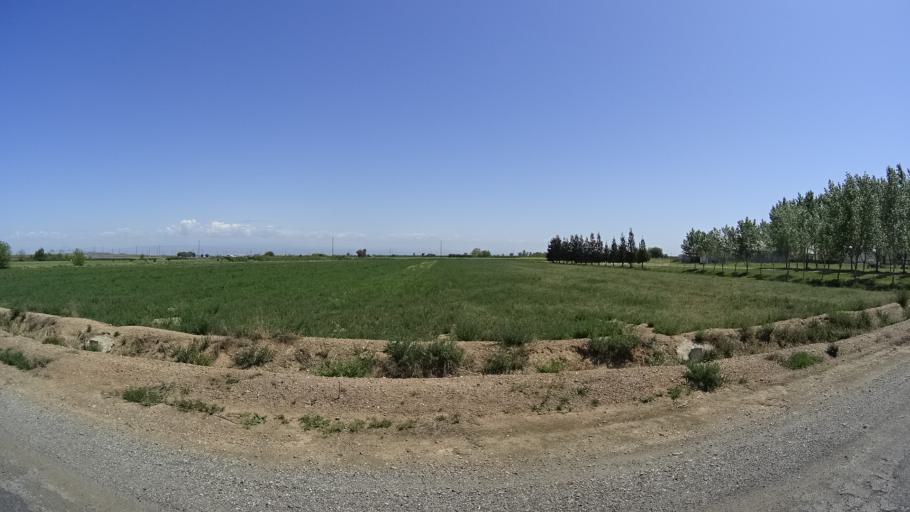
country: US
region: California
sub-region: Glenn County
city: Orland
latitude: 39.7715
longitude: -122.1504
